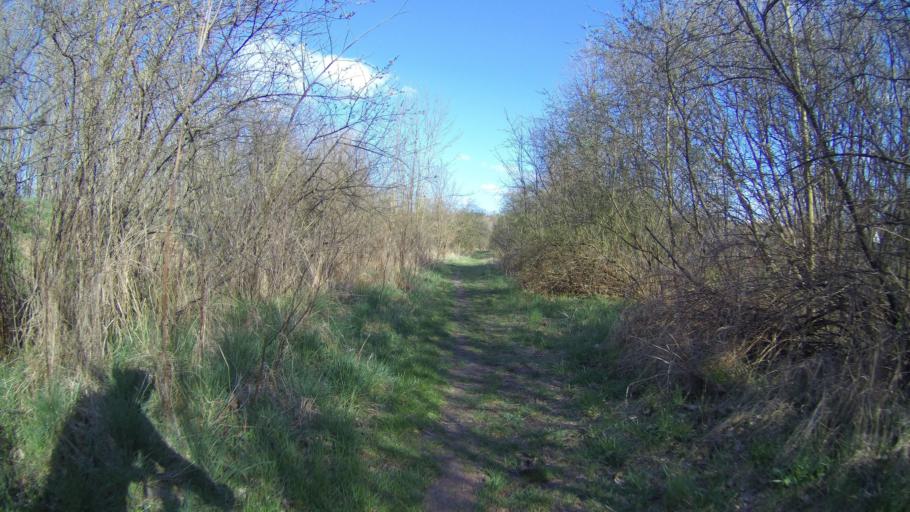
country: CZ
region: Ustecky
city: Zatec
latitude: 50.3276
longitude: 13.5261
